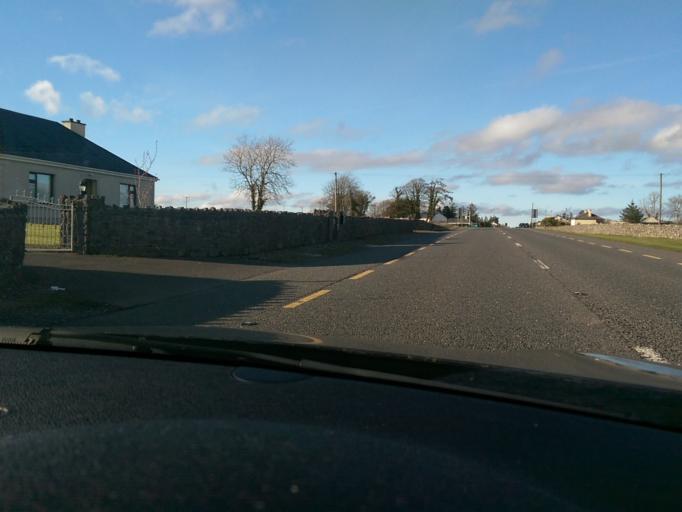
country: IE
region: Connaught
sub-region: Roscommon
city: Roscommon
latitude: 53.6625
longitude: -8.1982
